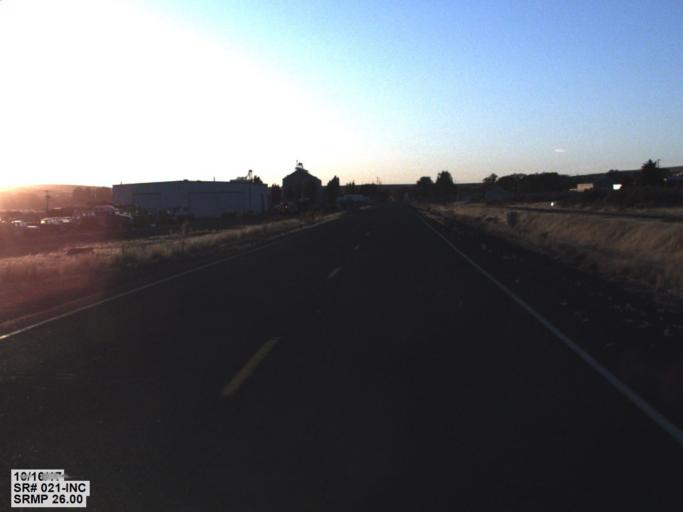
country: US
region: Washington
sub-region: Adams County
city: Ritzville
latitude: 46.9709
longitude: -118.6011
